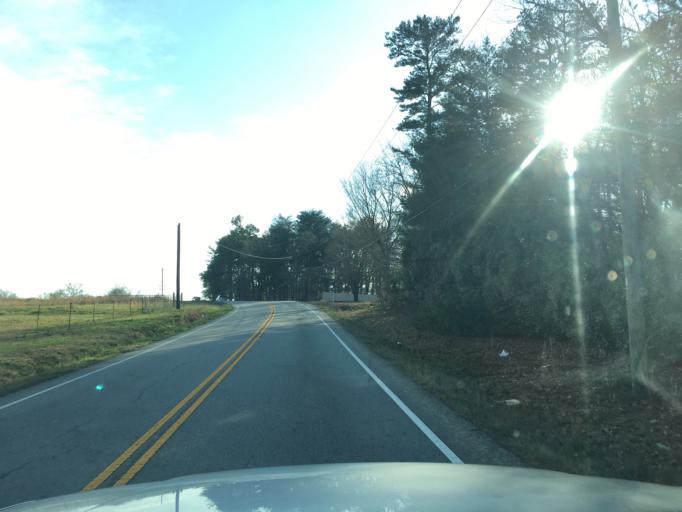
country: US
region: South Carolina
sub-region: Greenville County
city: Wade Hampton
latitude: 34.8729
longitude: -82.3098
